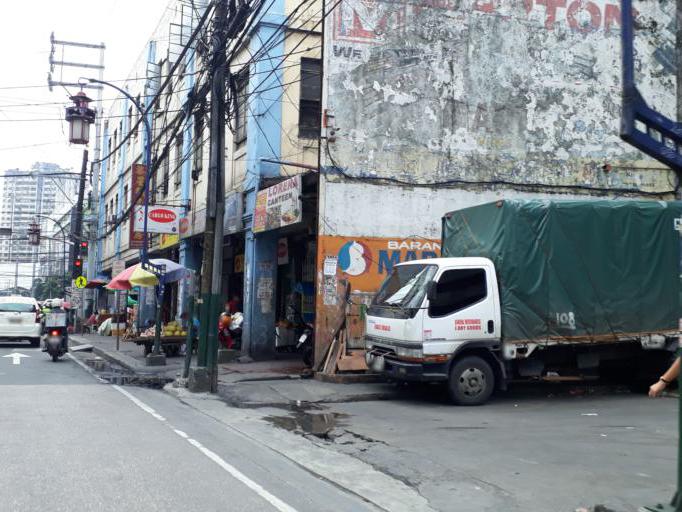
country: PH
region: Metro Manila
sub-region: City of Manila
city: Manila
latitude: 14.6052
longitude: 120.9746
